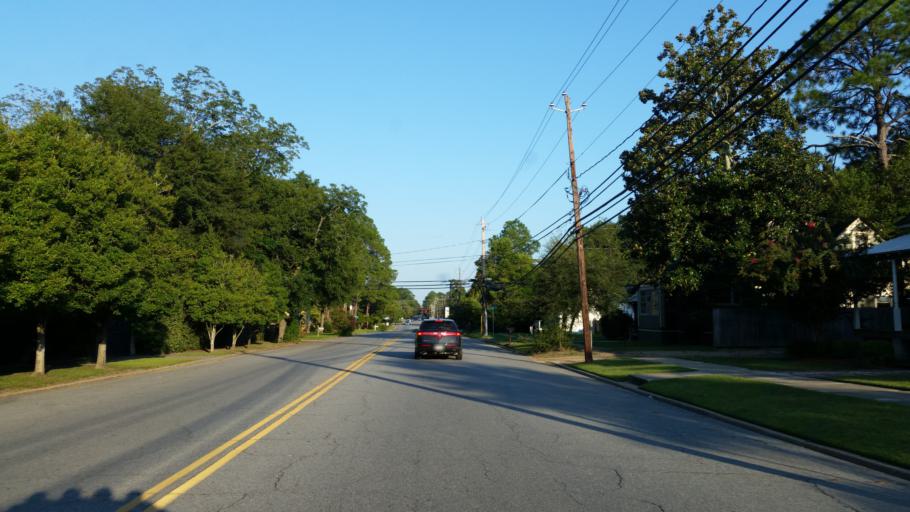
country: US
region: Georgia
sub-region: Tift County
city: Tifton
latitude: 31.4610
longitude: -83.5116
